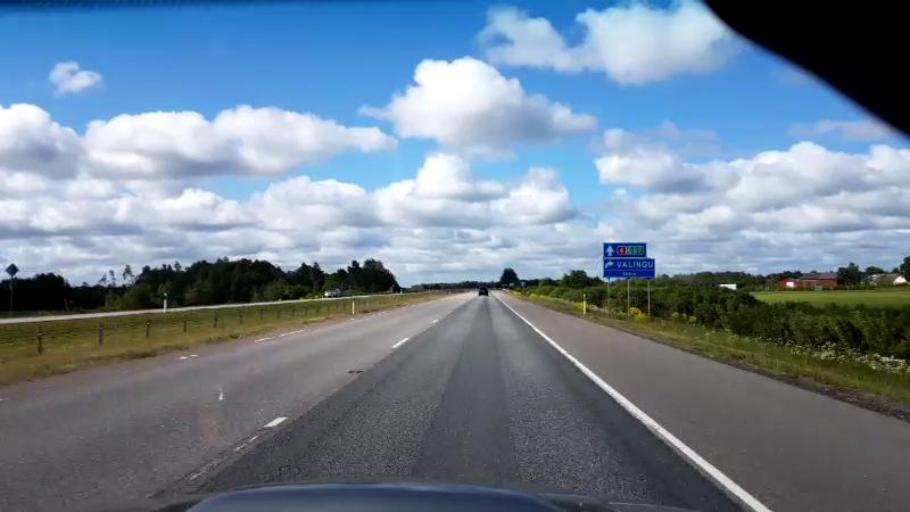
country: EE
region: Harju
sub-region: Saue linn
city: Saue
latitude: 59.2766
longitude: 24.5239
